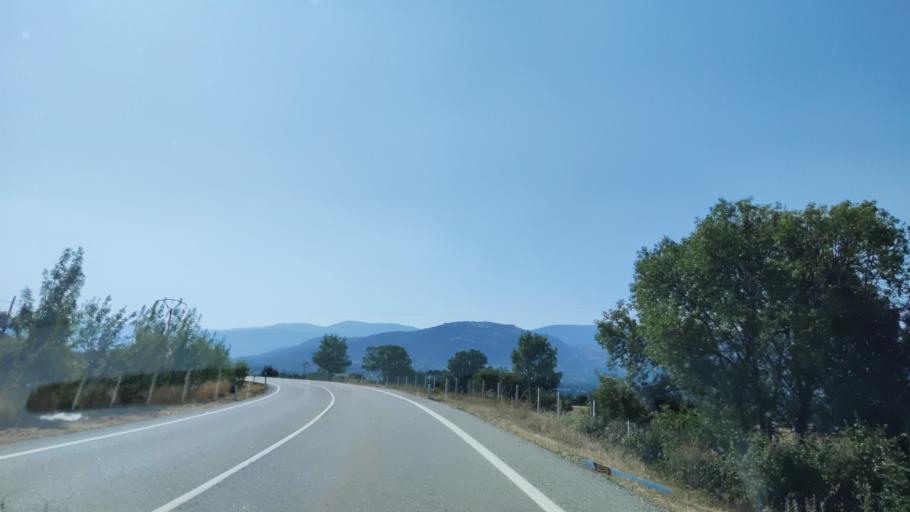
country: ES
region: Madrid
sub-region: Provincia de Madrid
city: Garganta de los Montes
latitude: 40.9438
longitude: -3.6861
